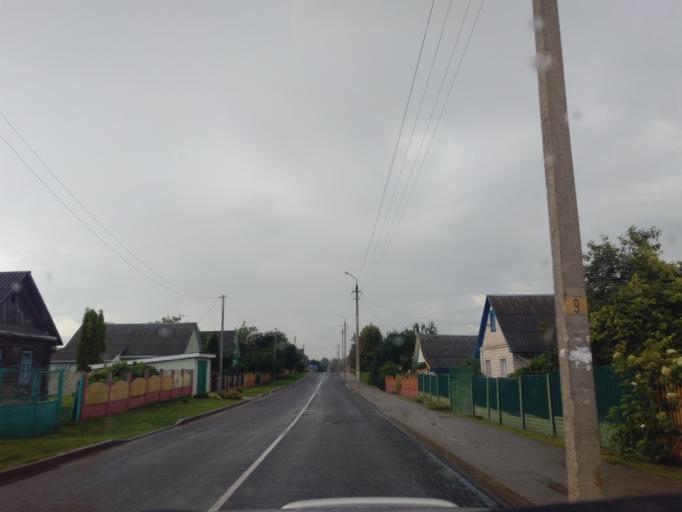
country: BY
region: Minsk
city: Kapyl'
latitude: 53.1539
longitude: 27.0897
